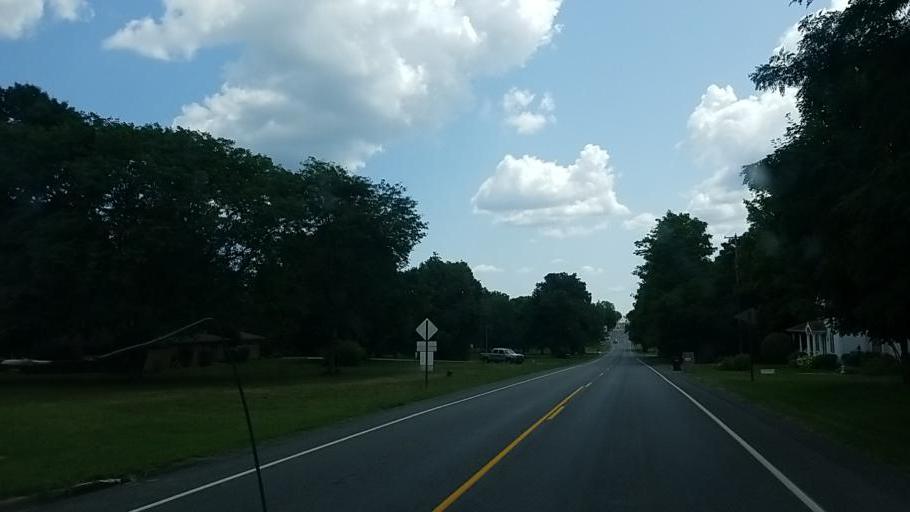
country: US
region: Michigan
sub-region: Kent County
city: Walker
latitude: 43.0300
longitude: -85.7361
